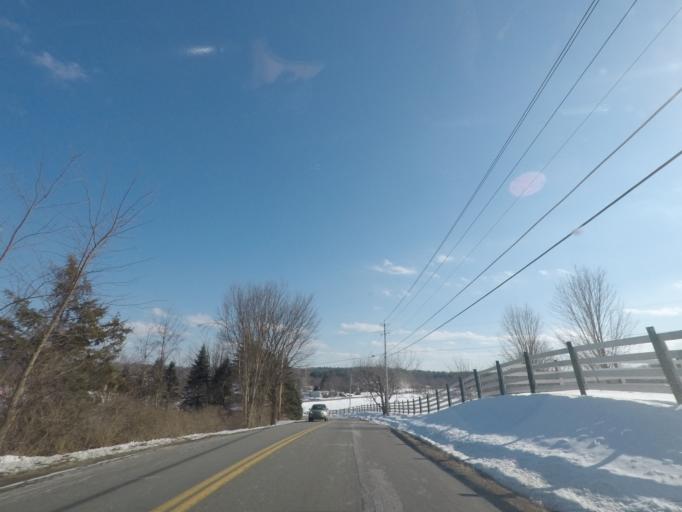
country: US
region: New York
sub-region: Rensselaer County
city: Hoosick Falls
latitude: 42.9016
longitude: -73.5025
